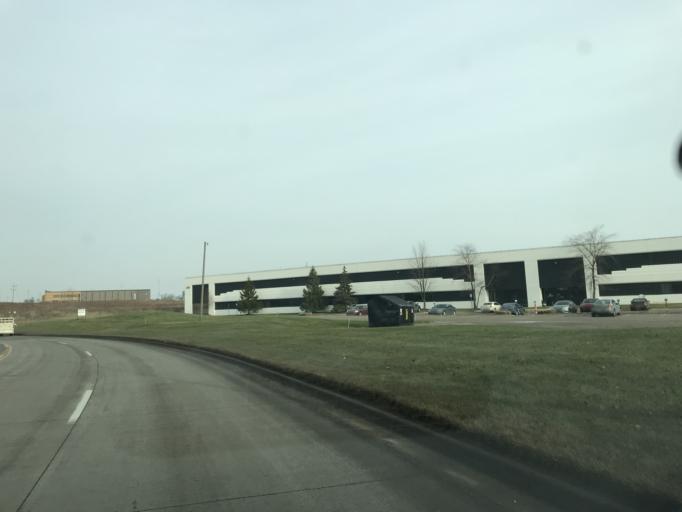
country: US
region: Michigan
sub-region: Ottawa County
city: Holland
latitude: 42.7503
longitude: -86.0757
